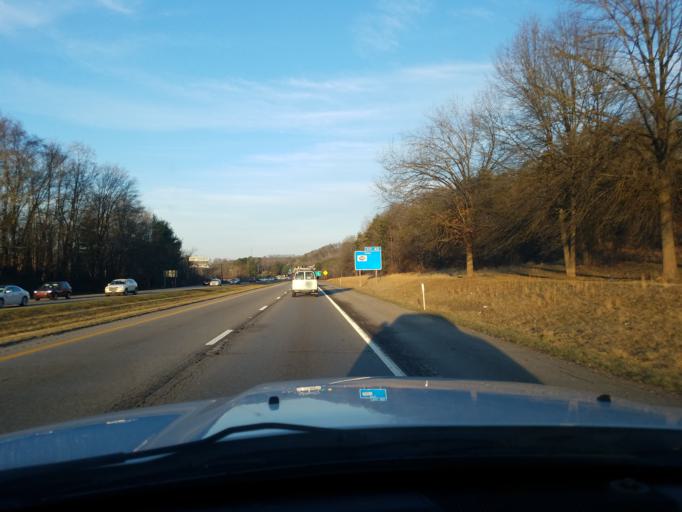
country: US
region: West Virginia
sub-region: Putnam County
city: Teays Valley
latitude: 38.4554
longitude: -81.8775
